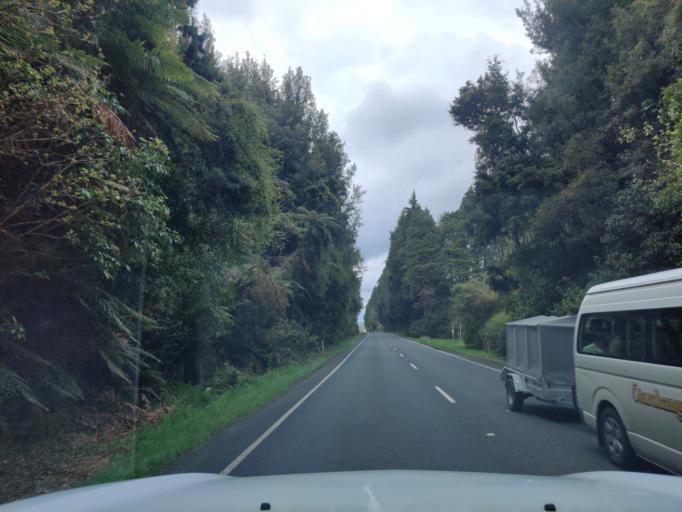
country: NZ
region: Waikato
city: Turangi
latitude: -38.9947
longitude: 175.3783
